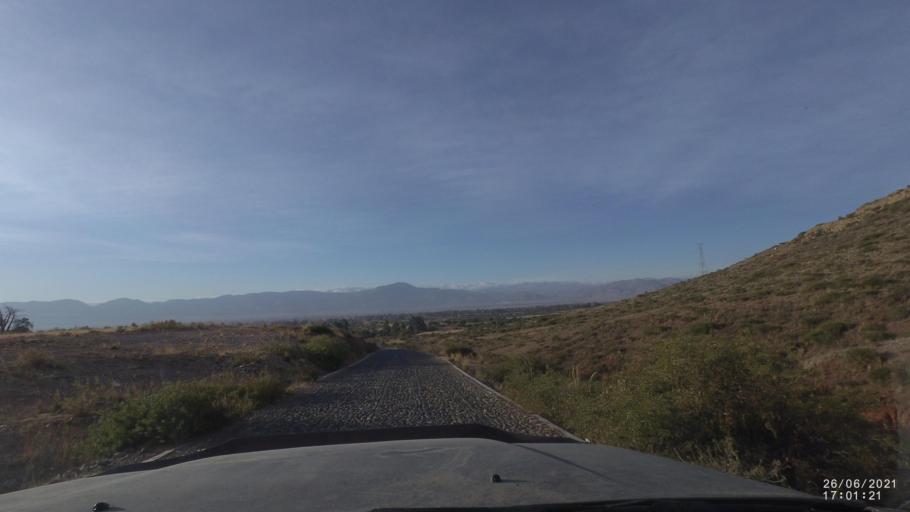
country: BO
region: Cochabamba
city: Cliza
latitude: -17.6622
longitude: -65.9111
